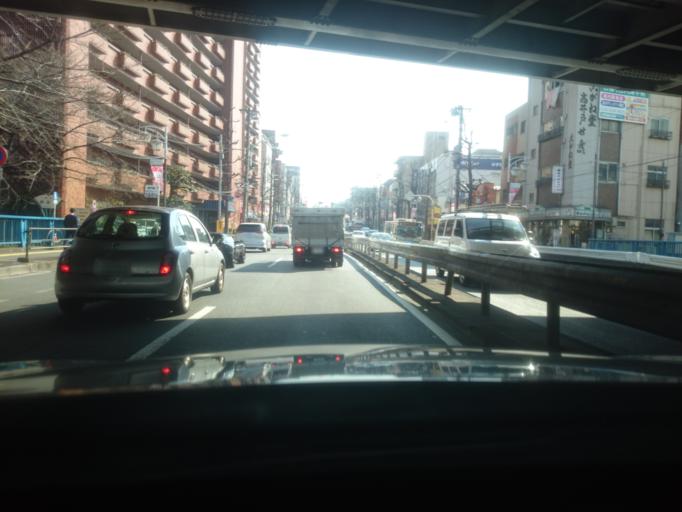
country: JP
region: Tokyo
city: Mitaka-shi
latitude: 35.6832
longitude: 139.6156
